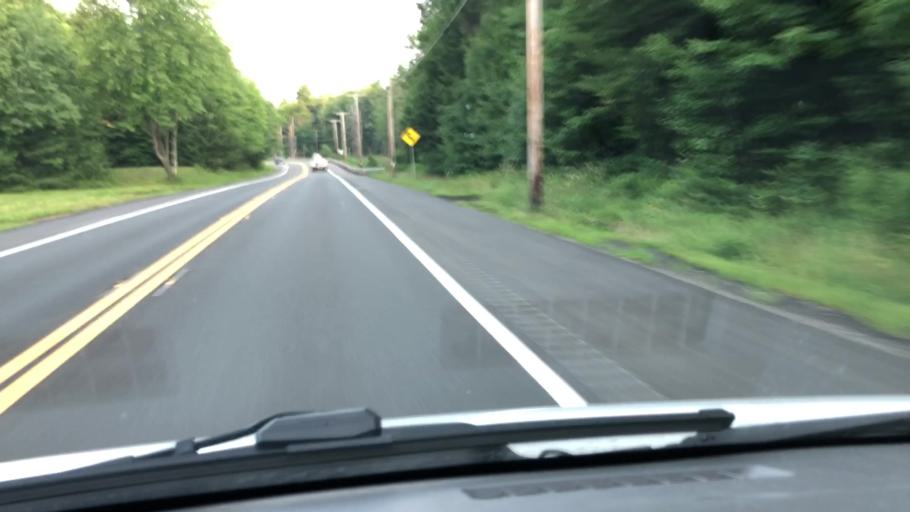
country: US
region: Massachusetts
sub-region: Hampshire County
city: Chesterfield
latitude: 42.4482
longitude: -72.8118
